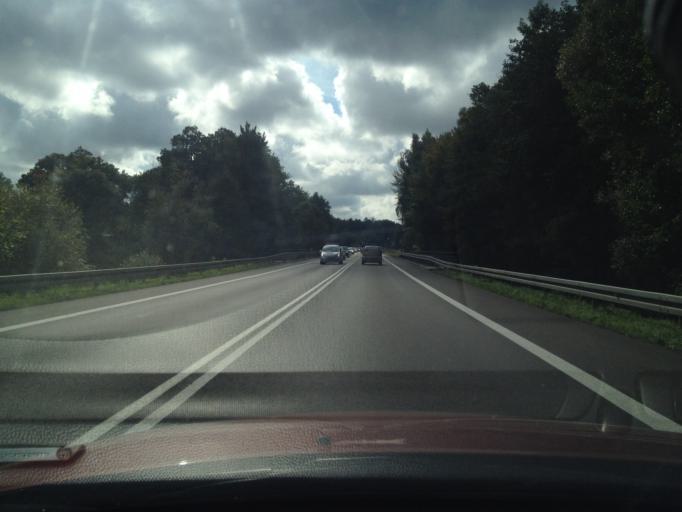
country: PL
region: West Pomeranian Voivodeship
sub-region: Powiat goleniowski
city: Przybiernow
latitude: 53.6806
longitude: 14.8097
